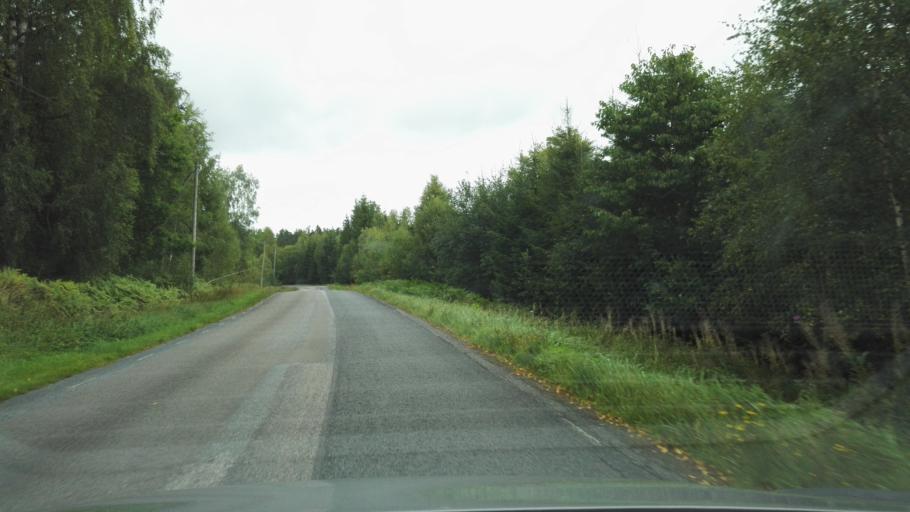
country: SE
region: Kronoberg
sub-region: Vaxjo Kommun
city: Rottne
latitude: 57.0746
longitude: 14.8211
